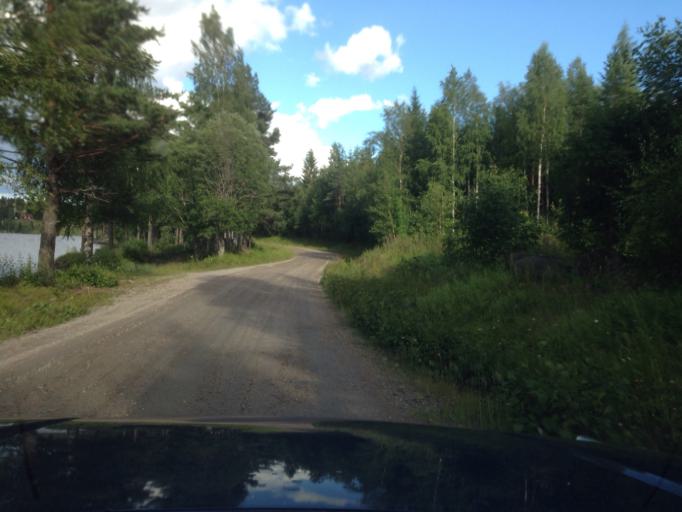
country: SE
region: Dalarna
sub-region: Ludvika Kommun
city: Abborrberget
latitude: 60.3113
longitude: 14.6621
